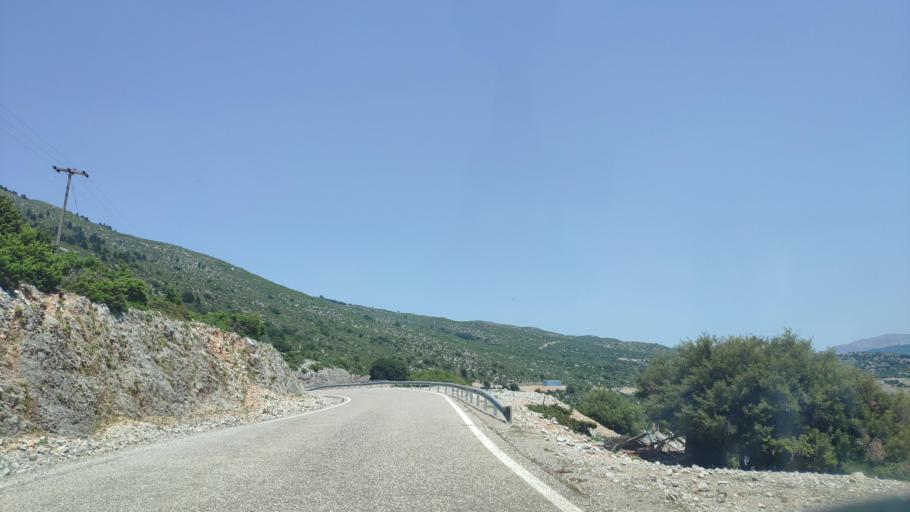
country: GR
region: West Greece
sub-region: Nomos Aitolias kai Akarnanias
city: Krikellos
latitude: 39.0617
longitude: 21.3828
